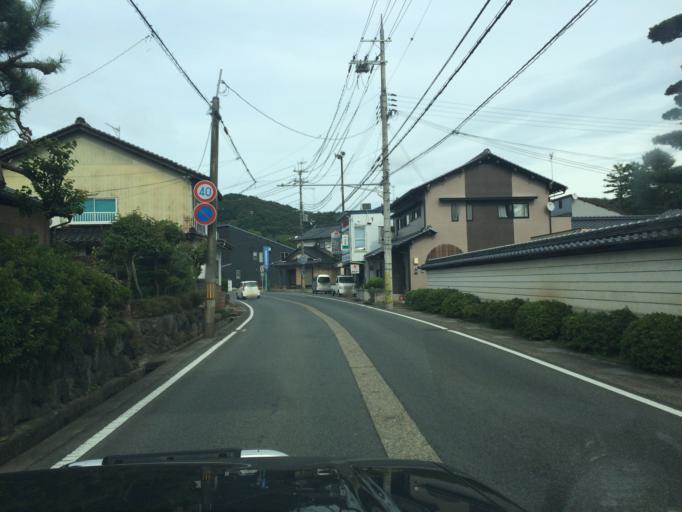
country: JP
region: Hyogo
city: Toyooka
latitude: 35.4627
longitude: 134.7743
